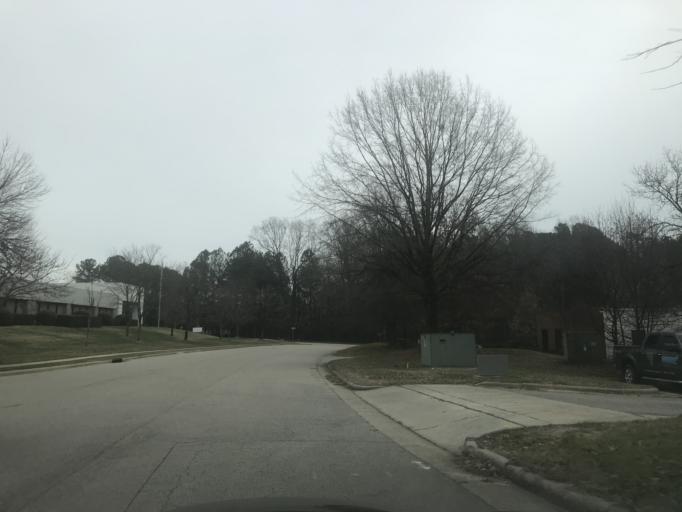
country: US
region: North Carolina
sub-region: Wake County
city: Raleigh
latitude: 35.8619
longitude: -78.5927
